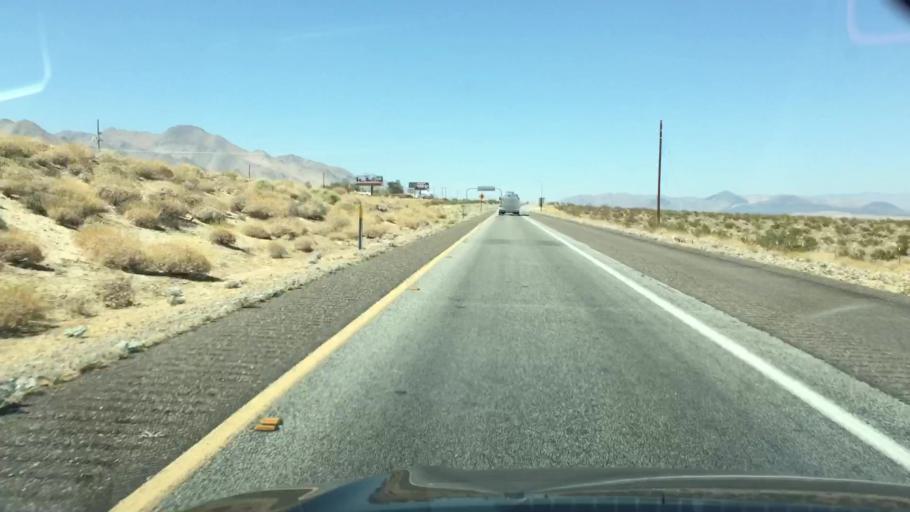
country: US
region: California
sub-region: Kern County
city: Inyokern
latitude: 35.6969
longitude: -117.8671
